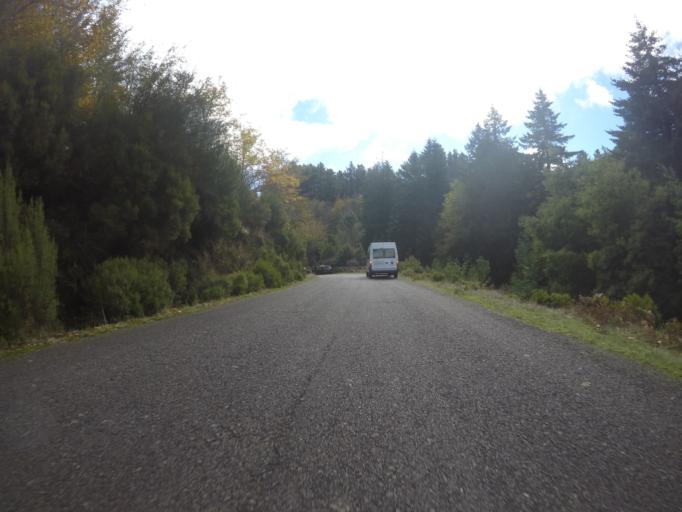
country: PT
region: Madeira
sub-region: Funchal
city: Nossa Senhora do Monte
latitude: 32.6988
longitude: -16.8846
